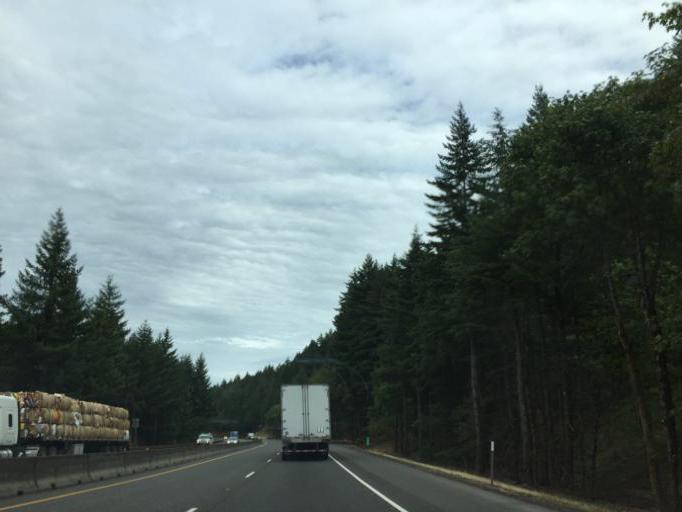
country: US
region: Oregon
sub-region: Hood River County
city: Cascade Locks
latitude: 45.6516
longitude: -121.9072
